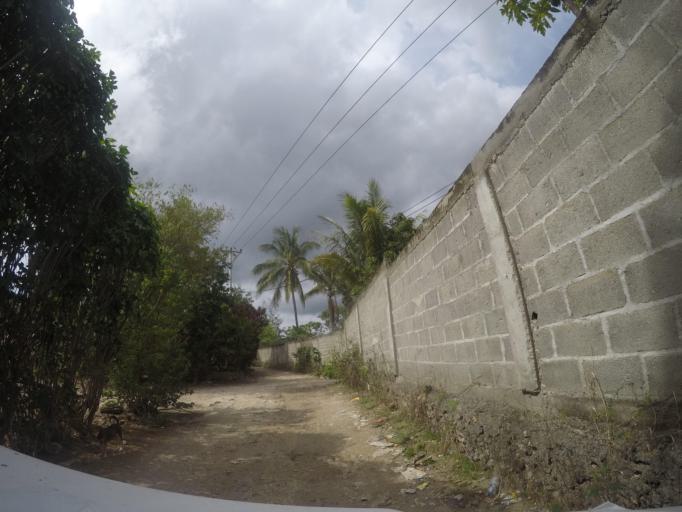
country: TL
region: Baucau
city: Baucau
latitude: -8.4696
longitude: 126.4566
